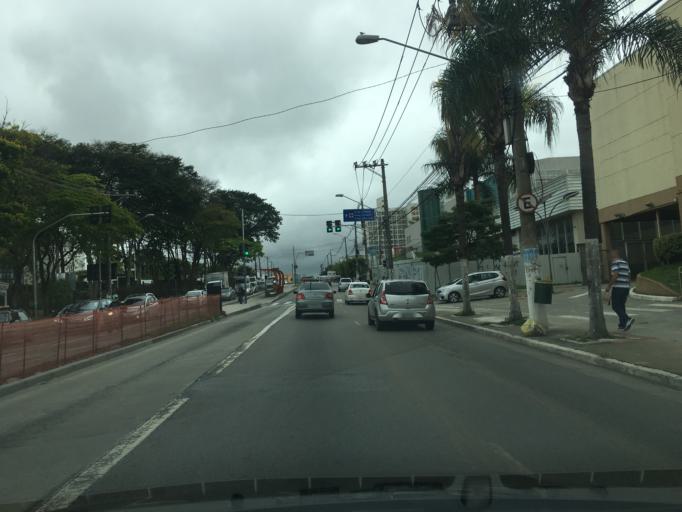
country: BR
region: Sao Paulo
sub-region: Taboao Da Serra
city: Taboao da Serra
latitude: -23.5863
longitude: -46.7237
